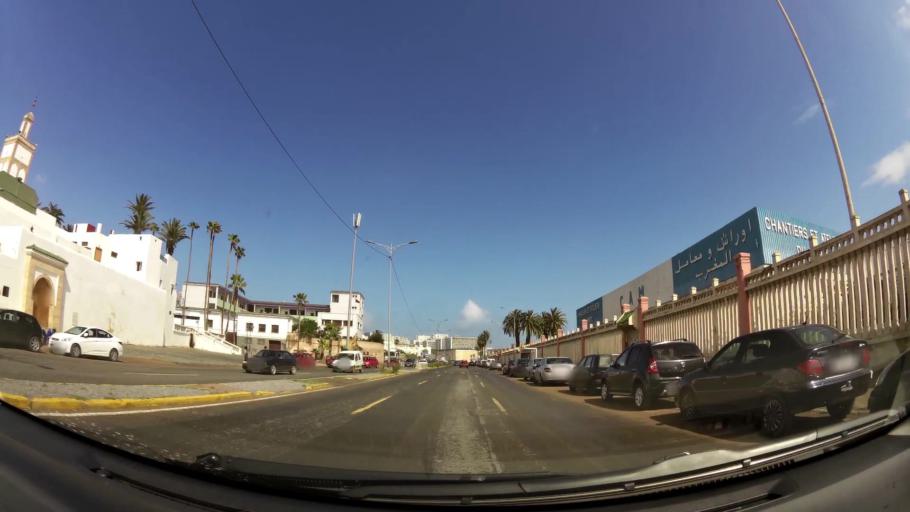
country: MA
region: Grand Casablanca
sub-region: Casablanca
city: Casablanca
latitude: 33.6015
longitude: -7.6178
